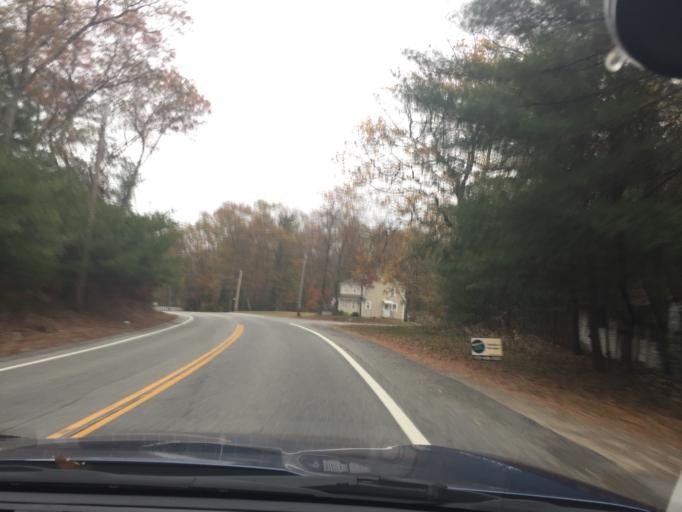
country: US
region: Rhode Island
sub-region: Providence County
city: North Scituate
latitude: 41.7920
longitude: -71.6261
